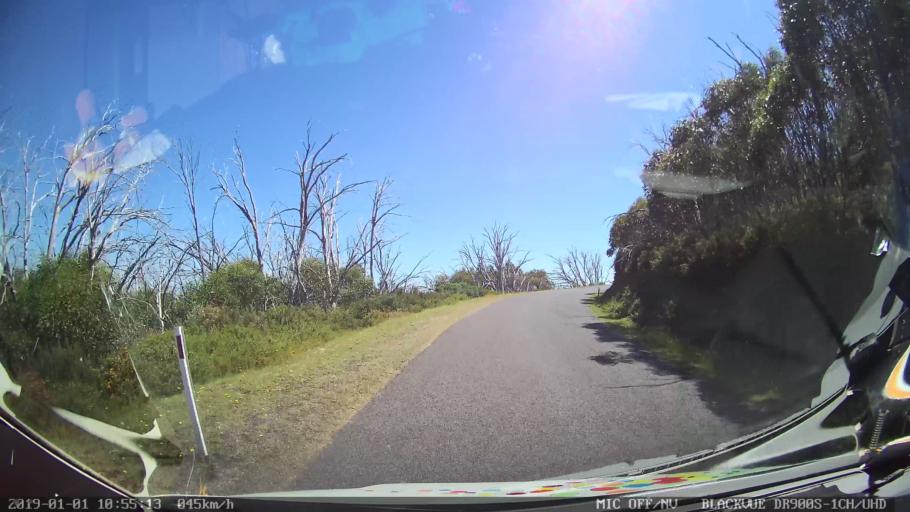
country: AU
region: New South Wales
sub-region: Snowy River
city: Jindabyne
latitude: -36.0091
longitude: 148.3875
